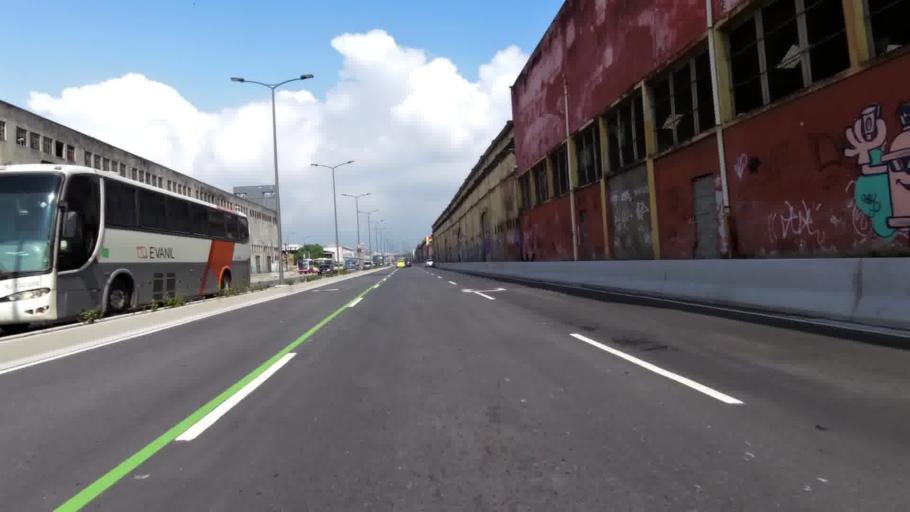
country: BR
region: Rio de Janeiro
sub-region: Rio De Janeiro
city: Rio de Janeiro
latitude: -22.8951
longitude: -43.2019
